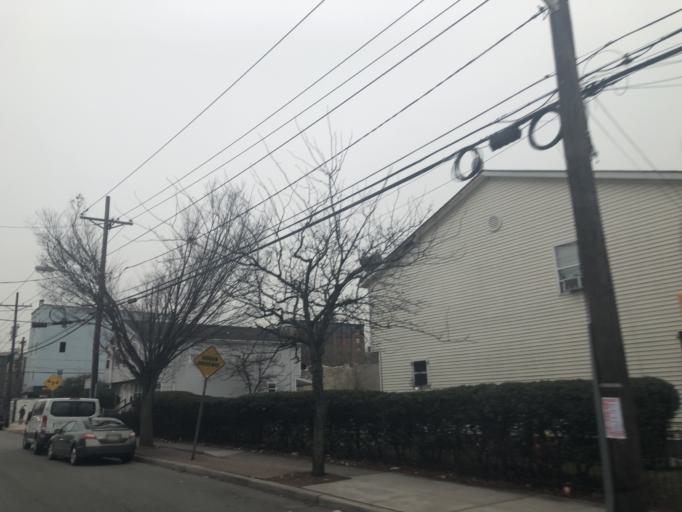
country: US
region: New Jersey
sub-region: Hudson County
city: Jersey City
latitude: 40.7140
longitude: -74.0589
